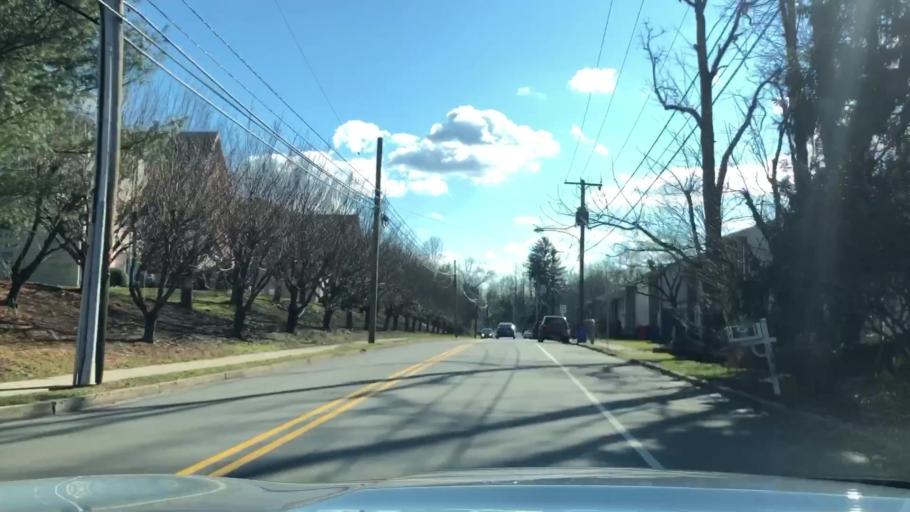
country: US
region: Pennsylvania
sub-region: Montgomery County
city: Pottstown
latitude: 40.2622
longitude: -75.6601
